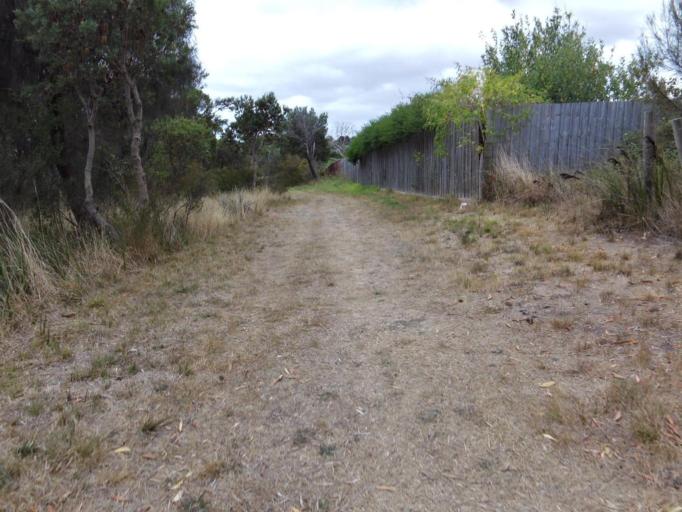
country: AU
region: Victoria
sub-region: Mornington Peninsula
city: Mount Martha
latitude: -38.2833
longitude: 145.0121
